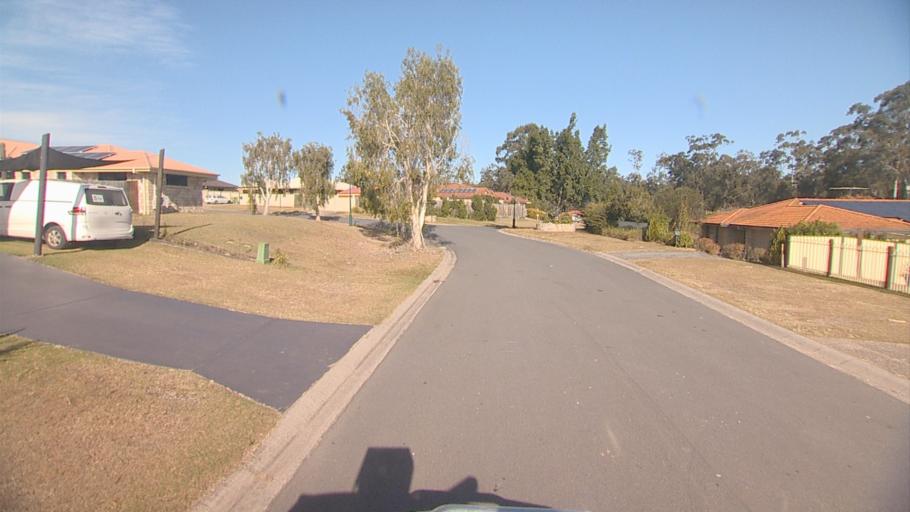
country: AU
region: Queensland
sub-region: Logan
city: North Maclean
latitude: -27.8100
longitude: 152.9503
